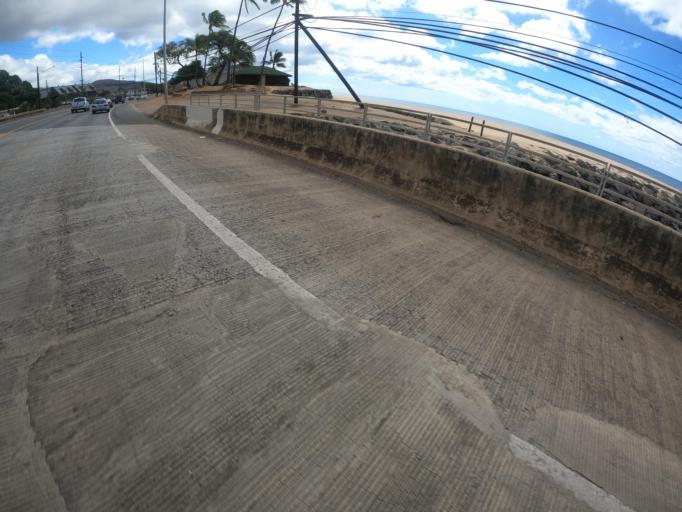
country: US
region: Hawaii
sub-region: Honolulu County
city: Ma'ili
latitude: 21.4286
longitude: -158.1796
